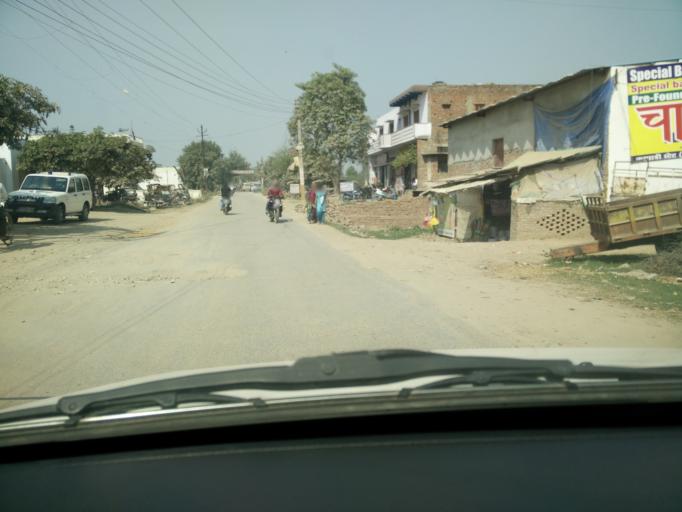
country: IN
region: Uttar Pradesh
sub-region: Varanasi
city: Ramnagar
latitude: 25.2659
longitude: 83.0162
